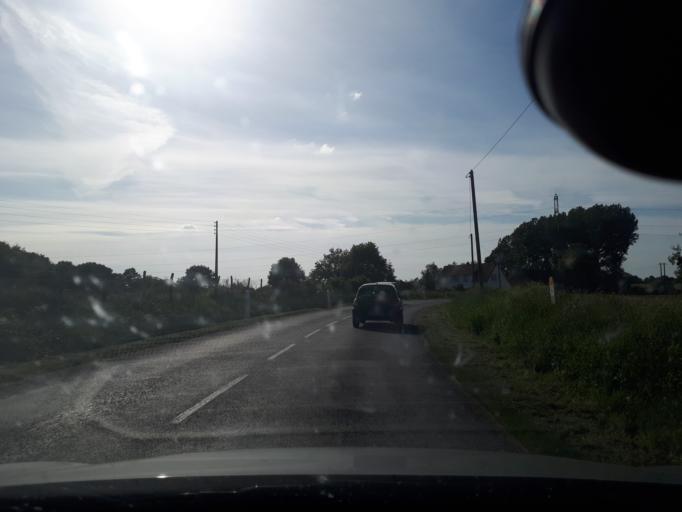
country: FR
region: Pays de la Loire
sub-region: Departement de la Sarthe
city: Champagne
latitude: 48.0776
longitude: 0.3274
